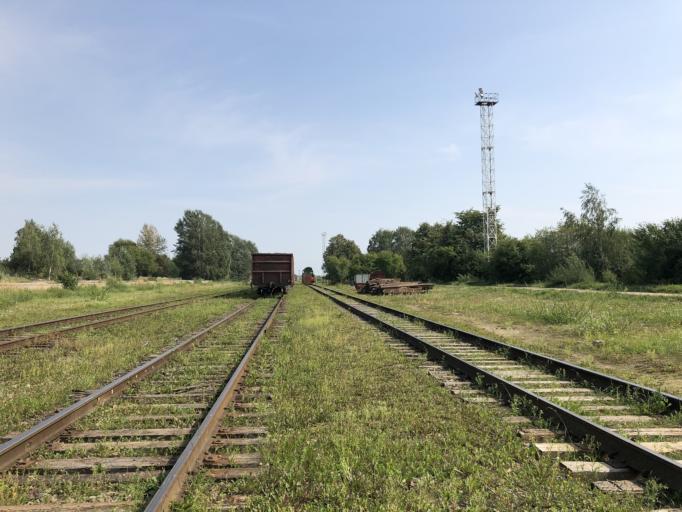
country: BY
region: Grodnenskaya
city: Hrodna
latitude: 53.7182
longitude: 23.8462
